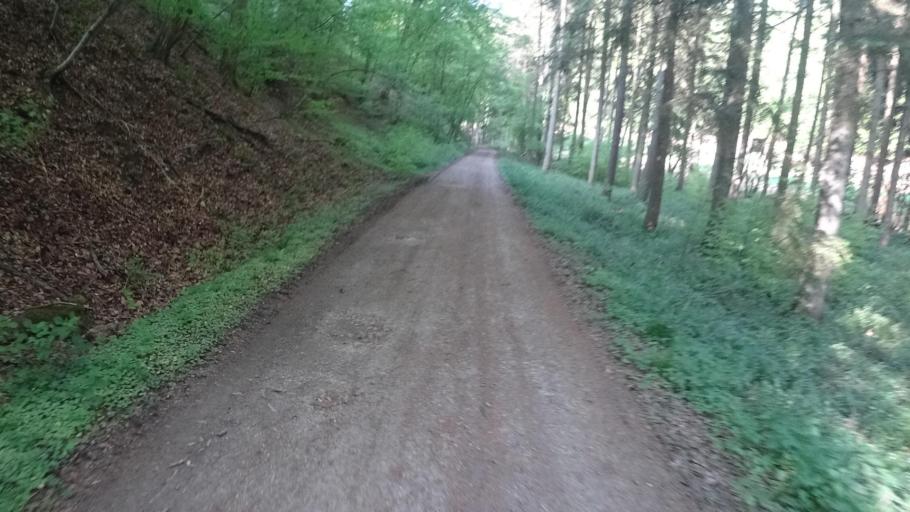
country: DE
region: Rheinland-Pfalz
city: Kirchsahr
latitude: 50.4955
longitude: 6.8979
